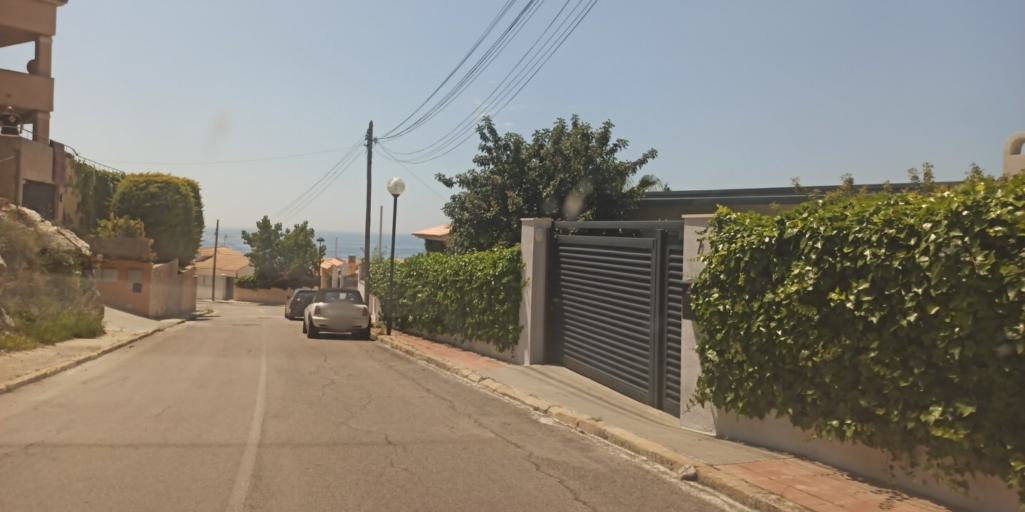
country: ES
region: Catalonia
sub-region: Provincia de Barcelona
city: Sitges
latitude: 41.2424
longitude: 1.8284
